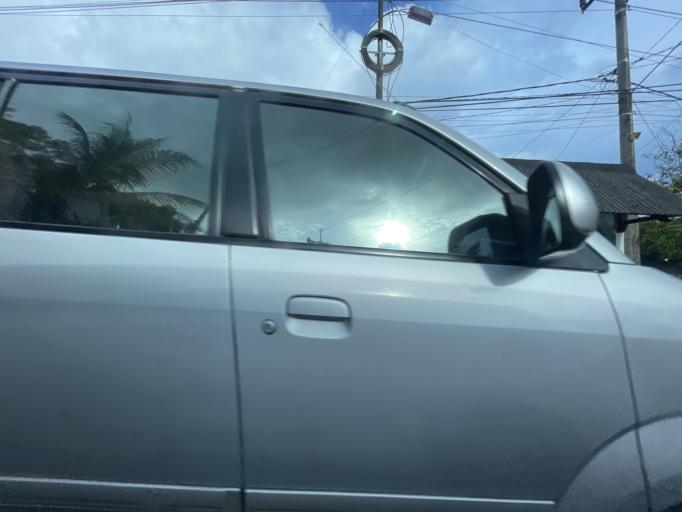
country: ID
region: Bali
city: Banjar Sedang
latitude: -8.5669
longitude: 115.2860
